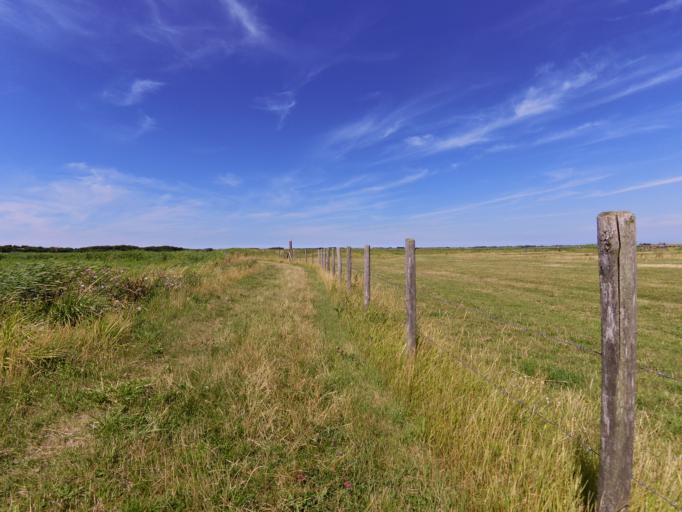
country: NL
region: South Holland
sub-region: Gemeente Goeree-Overflakkee
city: Ouddorp
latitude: 51.8002
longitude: 3.8714
